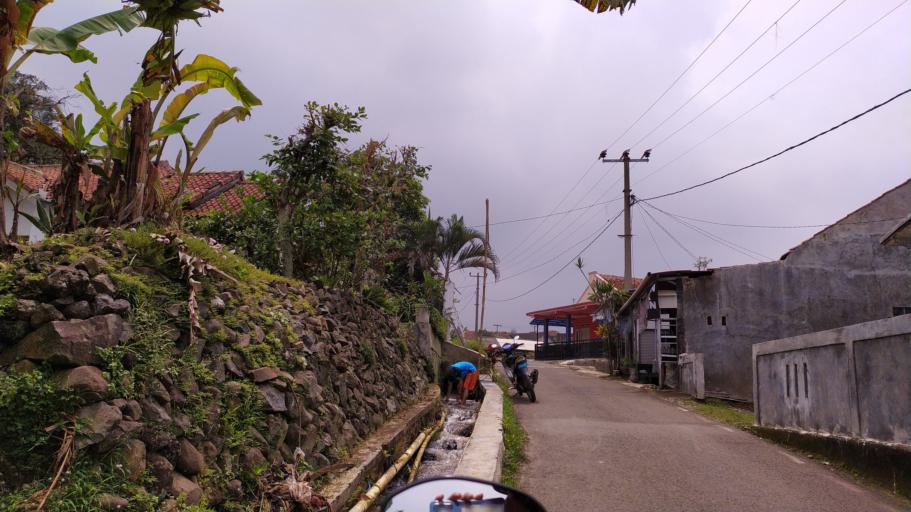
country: ID
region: West Java
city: Ciampea
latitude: -6.6174
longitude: 106.7104
